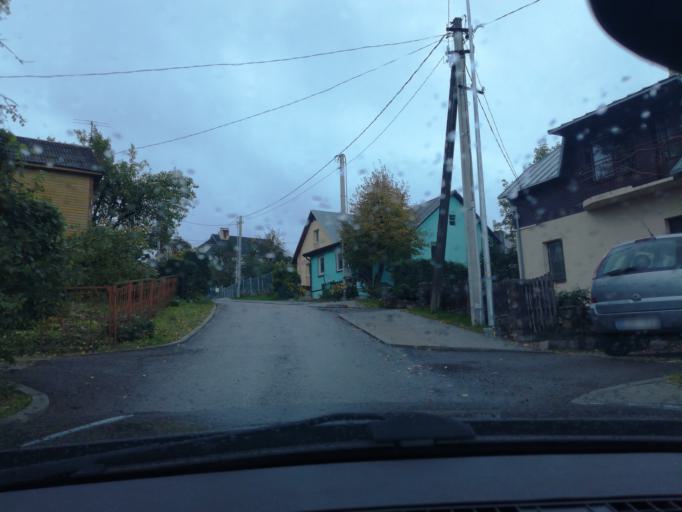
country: LT
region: Alytaus apskritis
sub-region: Alytus
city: Alytus
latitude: 54.4014
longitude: 24.0431
